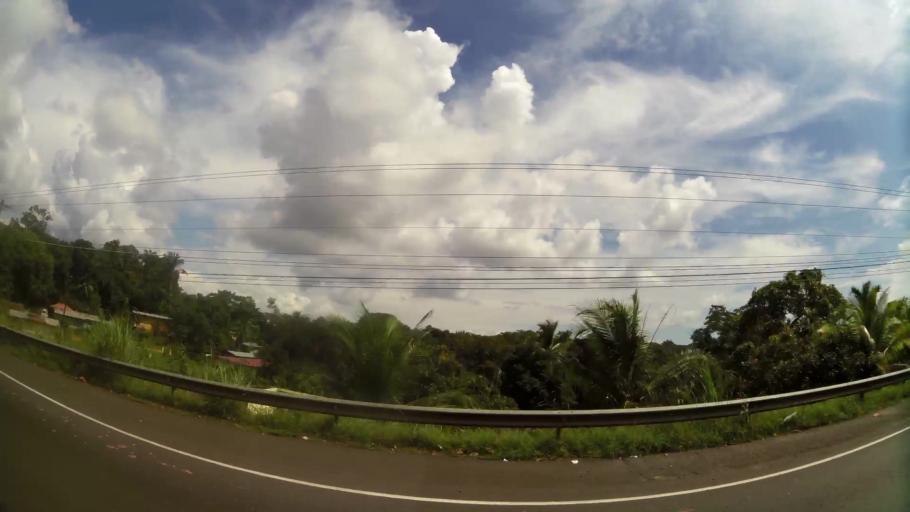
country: PA
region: Panama
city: Vista Alegre
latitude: 8.9438
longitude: -79.6803
